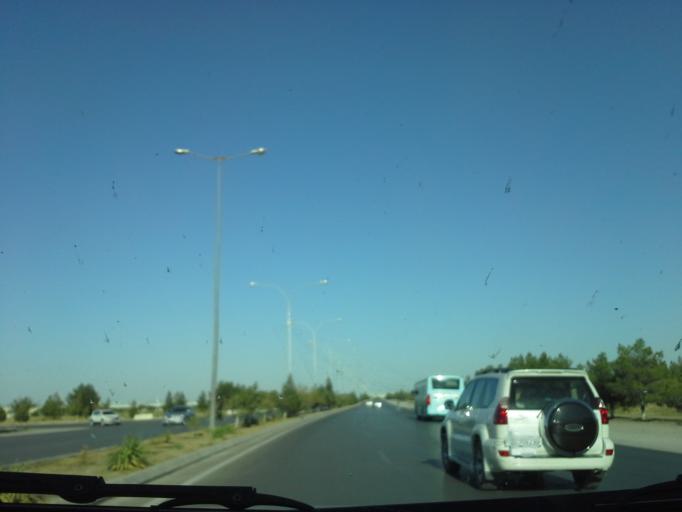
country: TM
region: Ahal
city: Ashgabat
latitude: 37.9709
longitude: 58.2819
